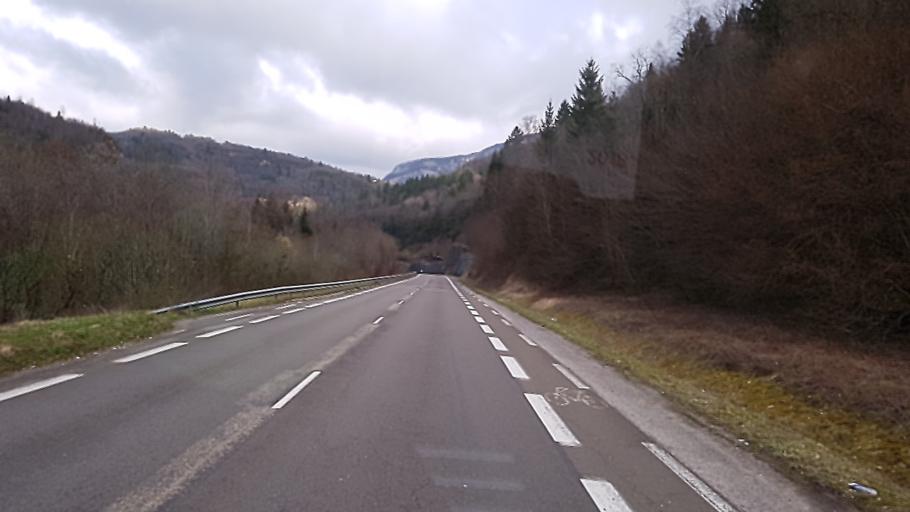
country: FR
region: Franche-Comte
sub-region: Departement du Jura
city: Lavans-les-Saint-Claude
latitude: 46.3610
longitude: 5.7944
